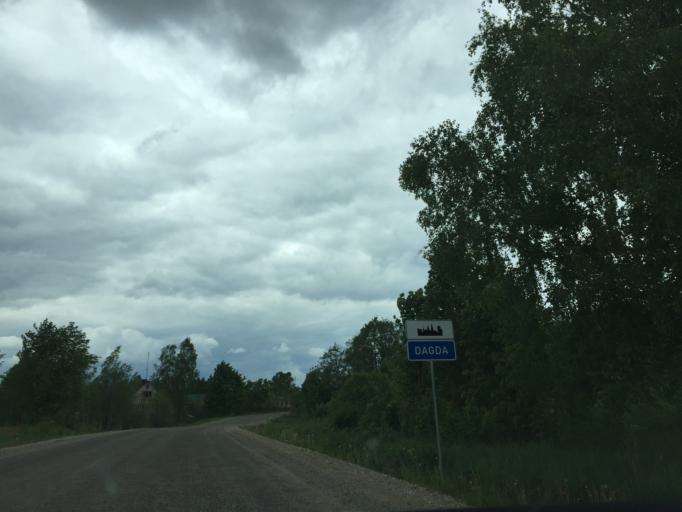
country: LV
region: Dagda
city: Dagda
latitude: 56.0841
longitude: 27.5313
